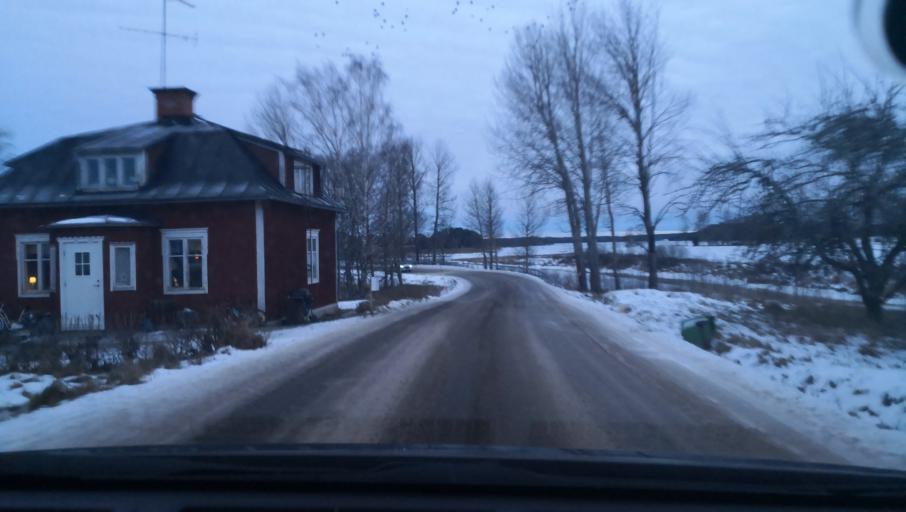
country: SE
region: Dalarna
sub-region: Avesta Kommun
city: Horndal
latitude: 60.2001
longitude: 16.4908
